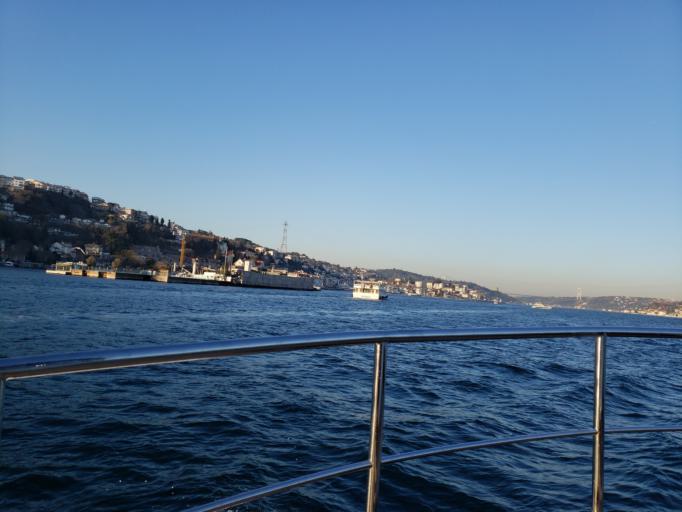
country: TR
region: Istanbul
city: UEskuedar
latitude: 41.0574
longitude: 29.0398
